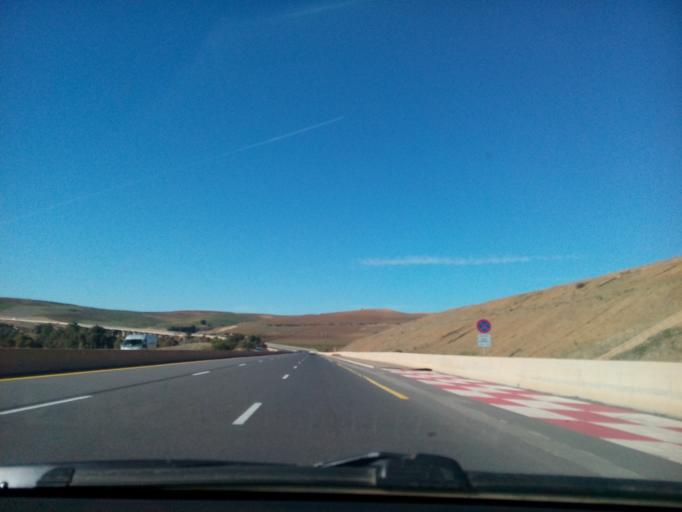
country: DZ
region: Tlemcen
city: Sidi Abdelli
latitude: 35.0390
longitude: -1.0584
